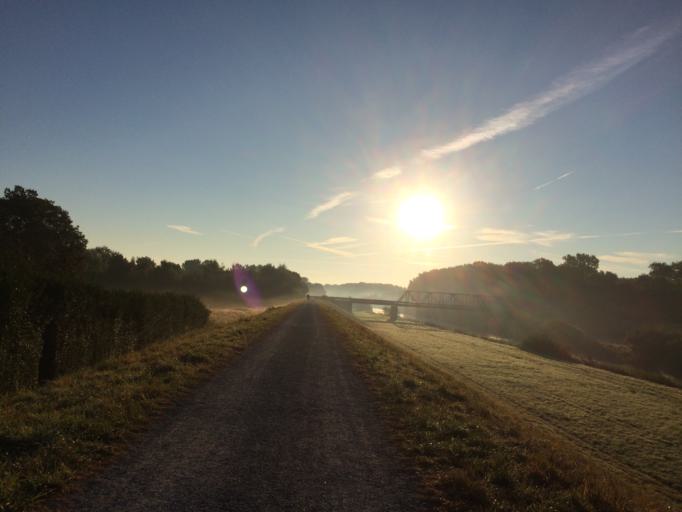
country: DE
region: North Rhine-Westphalia
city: Dorsten
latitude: 51.6660
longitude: 6.9872
